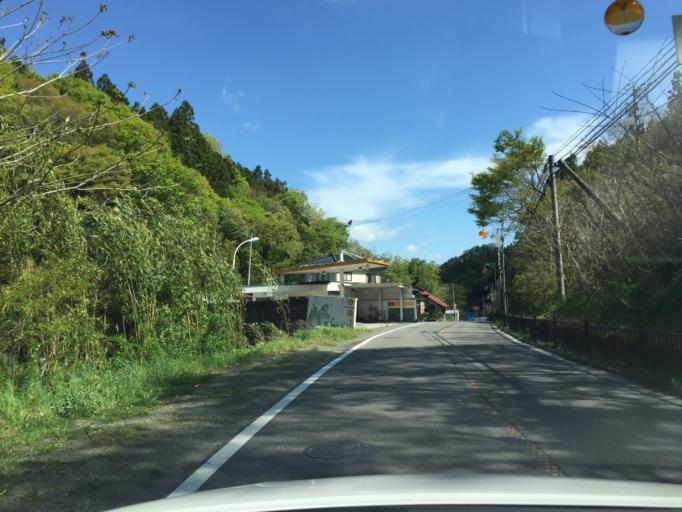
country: JP
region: Fukushima
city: Nihommatsu
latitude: 37.5650
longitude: 140.5083
